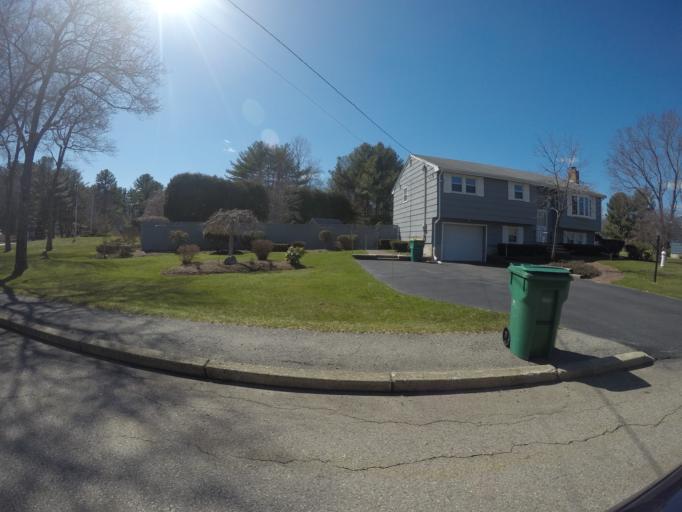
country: US
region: Massachusetts
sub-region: Bristol County
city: Easton
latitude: 42.0092
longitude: -71.1004
